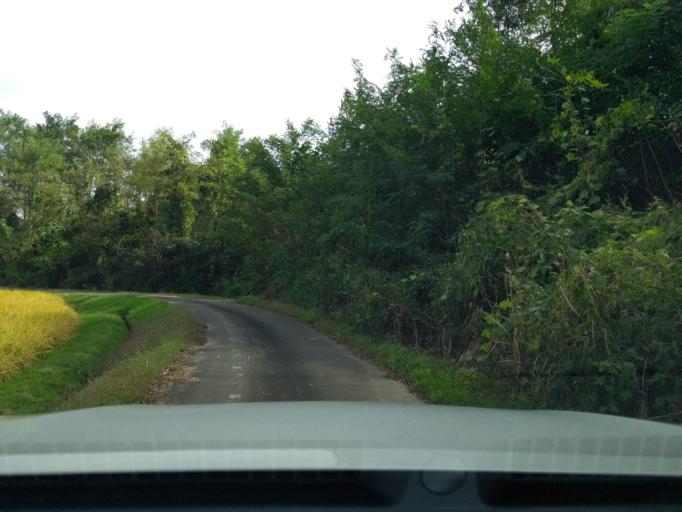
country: JP
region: Fukushima
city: Koriyama
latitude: 37.4126
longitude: 140.2988
